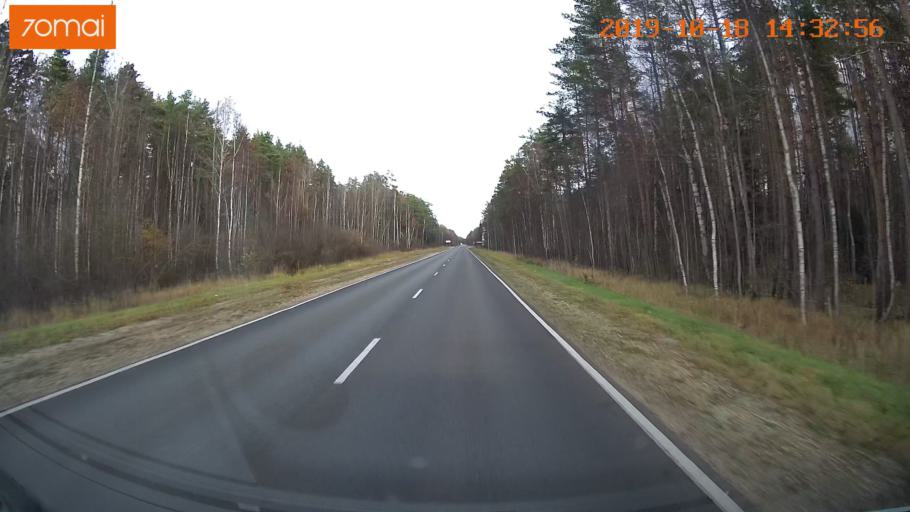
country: RU
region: Rjazan
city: Tuma
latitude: 55.1959
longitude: 40.5877
